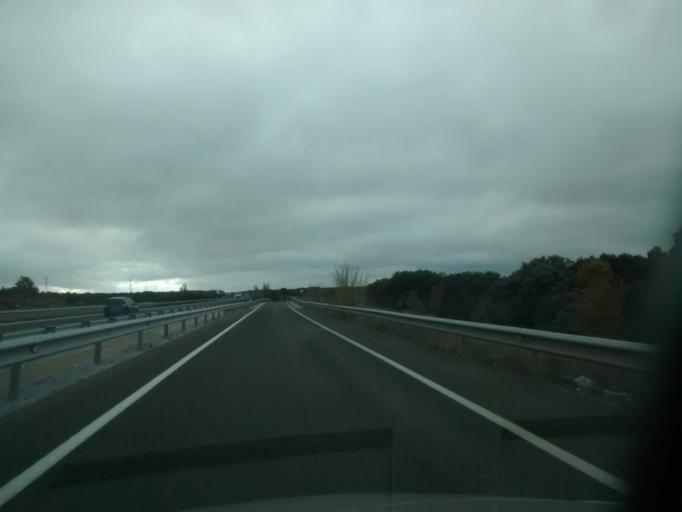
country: ES
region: Castille-La Mancha
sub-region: Provincia de Guadalajara
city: Sauca
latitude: 41.0119
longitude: -2.5569
